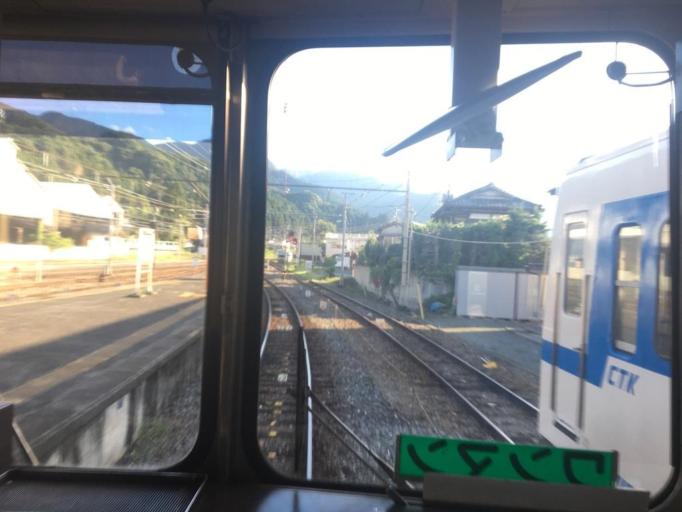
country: JP
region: Saitama
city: Chichibu
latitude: 35.9721
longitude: 139.0683
